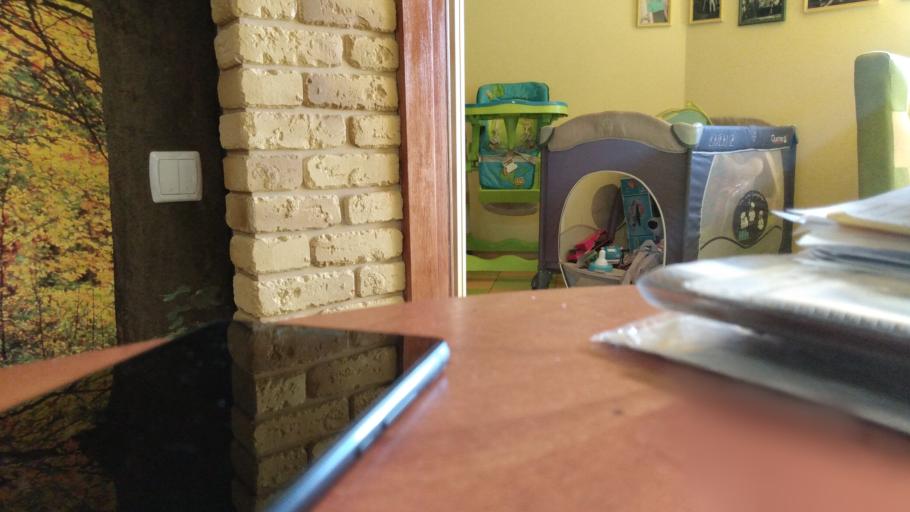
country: RU
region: Tverskaya
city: Vyshniy Volochek
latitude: 57.7235
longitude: 34.5743
